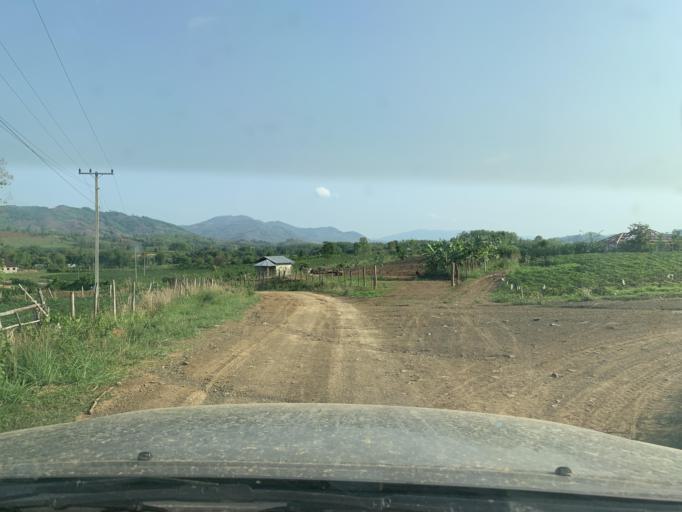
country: TH
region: Uttaradit
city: Ban Khok
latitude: 18.2735
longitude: 101.3062
